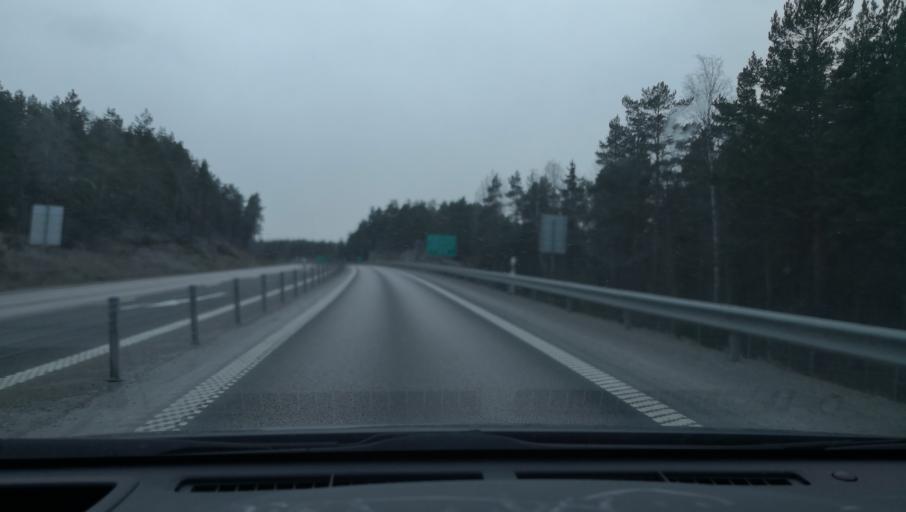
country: SE
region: Soedermanland
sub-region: Strangnas Kommun
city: Strangnas
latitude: 59.3748
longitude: 16.9662
